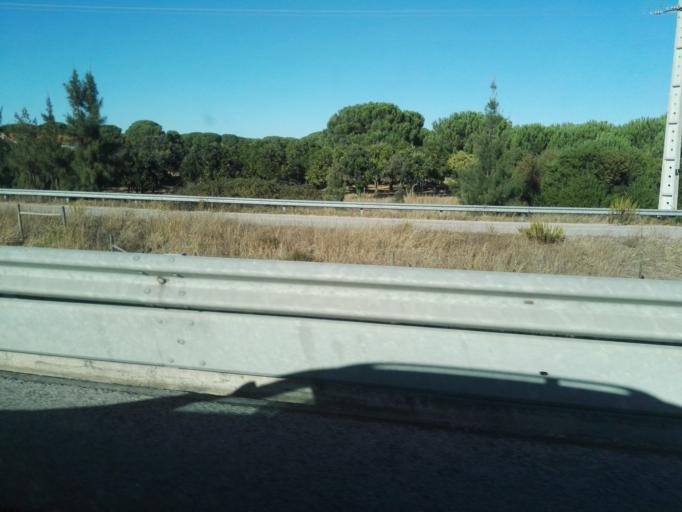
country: PT
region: Santarem
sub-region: Benavente
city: Benavente
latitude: 38.9568
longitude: -8.8285
